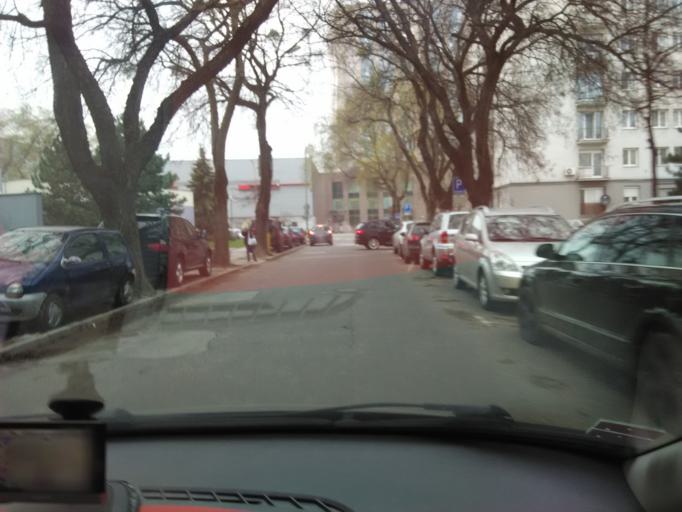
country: SK
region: Bratislavsky
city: Bratislava
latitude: 48.1595
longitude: 17.1390
